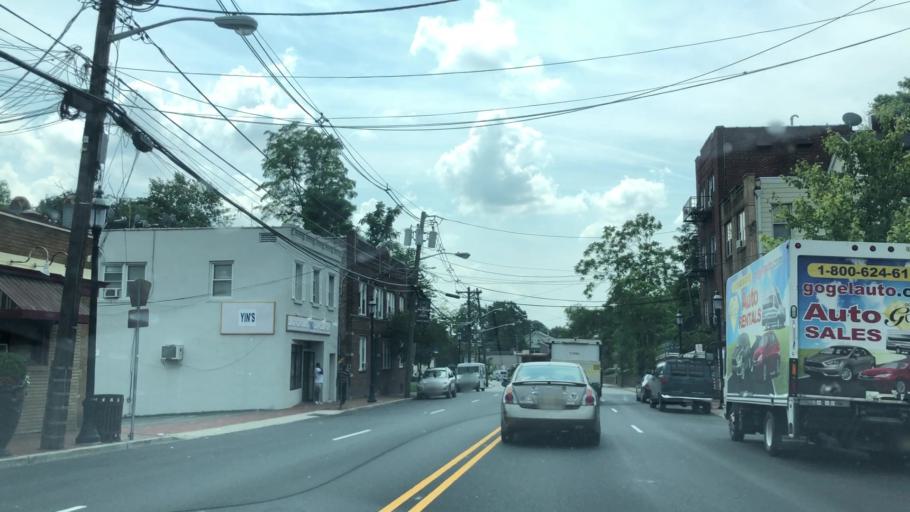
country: US
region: New Jersey
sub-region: Essex County
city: West Orange
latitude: 40.7926
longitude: -74.2331
